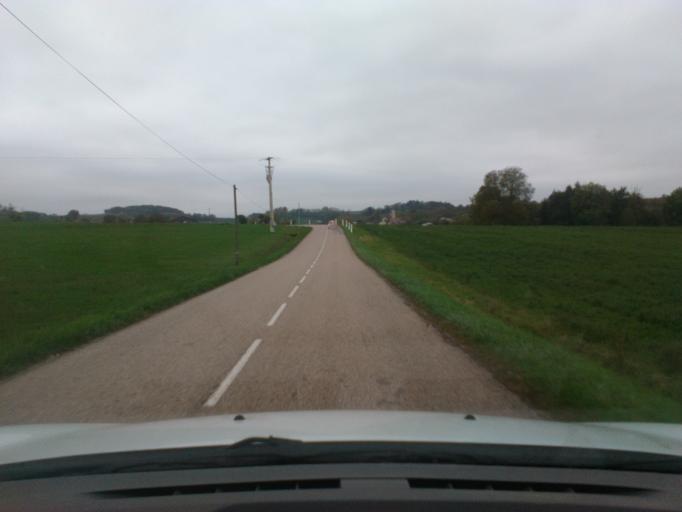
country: FR
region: Lorraine
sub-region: Departement des Vosges
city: Vincey
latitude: 48.3050
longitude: 6.2823
